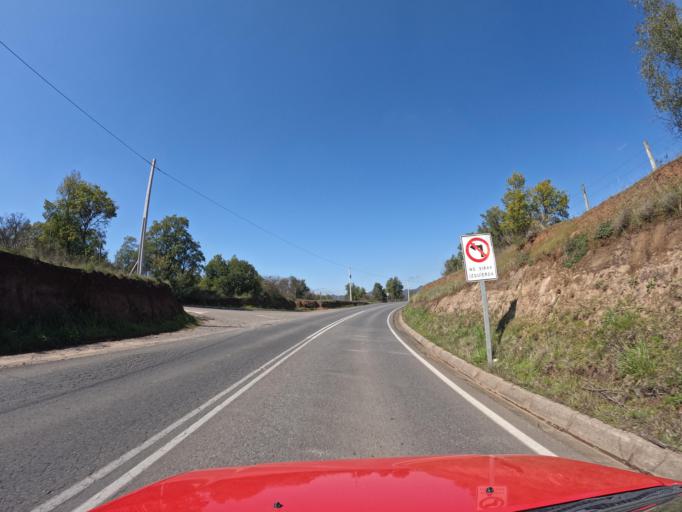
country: CL
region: Maule
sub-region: Provincia de Talca
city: San Clemente
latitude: -35.4756
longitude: -71.2708
